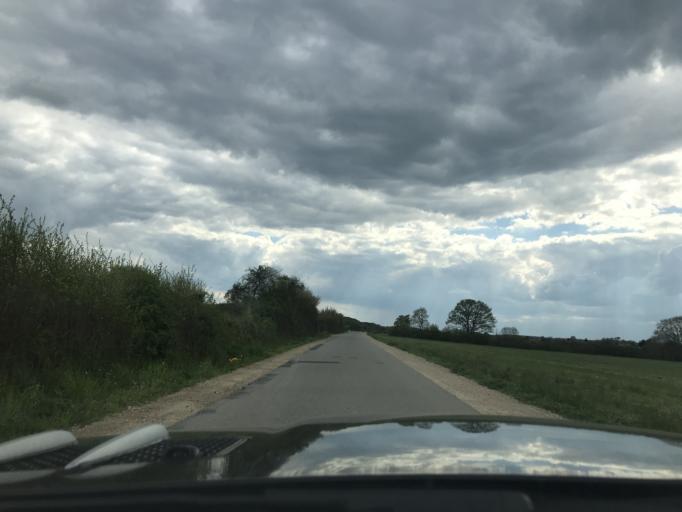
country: DE
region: Schleswig-Holstein
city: Gross Gronau
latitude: 53.7759
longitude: 10.7789
